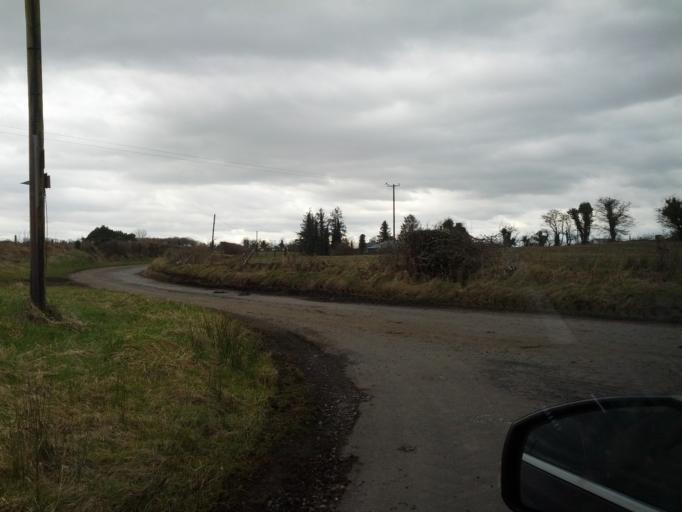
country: IE
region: Connaught
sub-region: County Galway
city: Athenry
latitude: 53.3877
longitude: -8.6386
